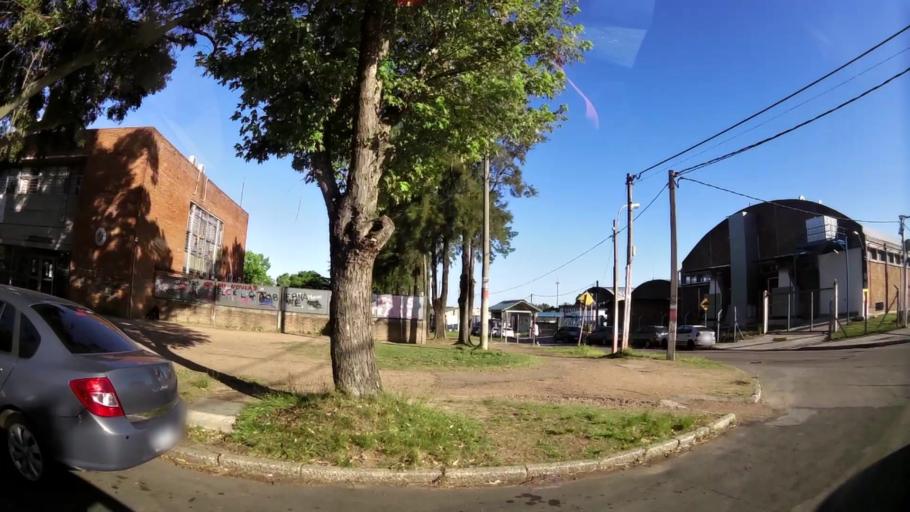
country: UY
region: Canelones
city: La Paz
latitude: -34.8295
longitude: -56.2029
